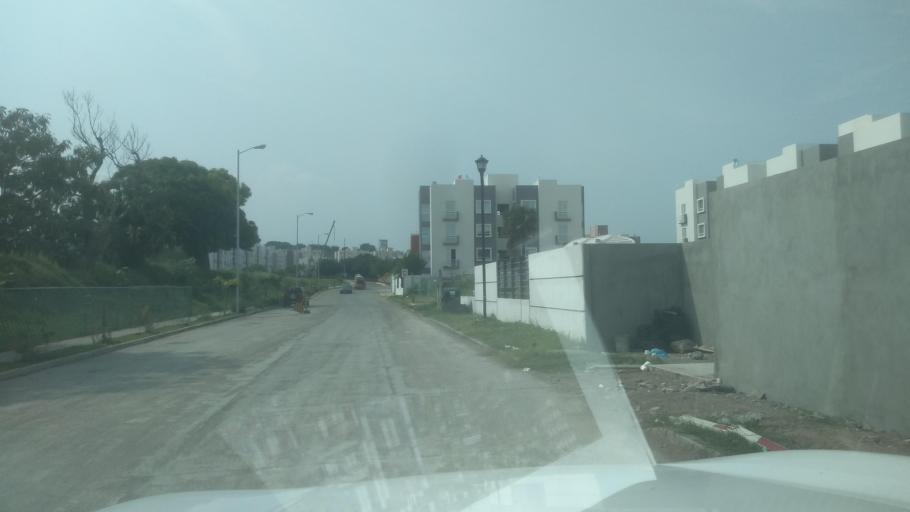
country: MX
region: Veracruz
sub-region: Veracruz
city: Lomas de Rio Medio Cuatro
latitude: 19.1773
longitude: -96.2080
